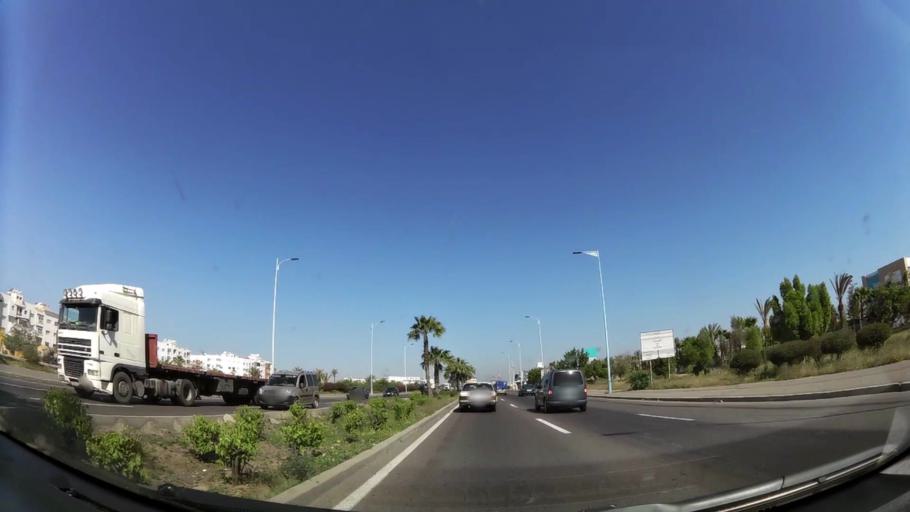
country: MA
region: Oued ed Dahab-Lagouira
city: Dakhla
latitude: 30.4029
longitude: -9.5311
